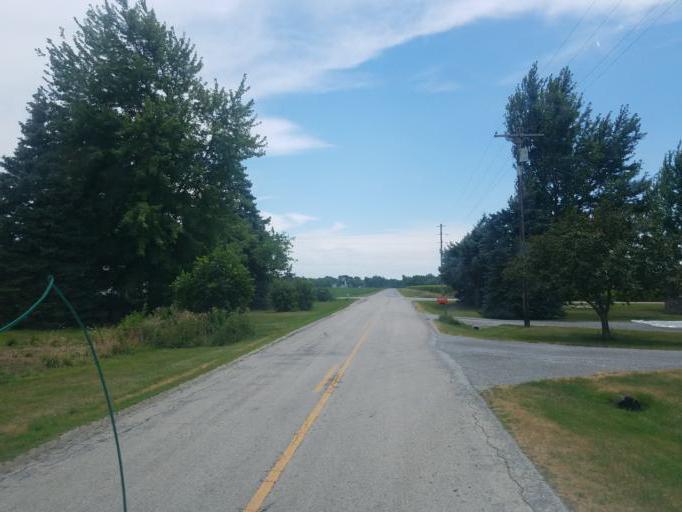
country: US
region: Ohio
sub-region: Paulding County
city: Antwerp
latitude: 41.2088
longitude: -84.7276
